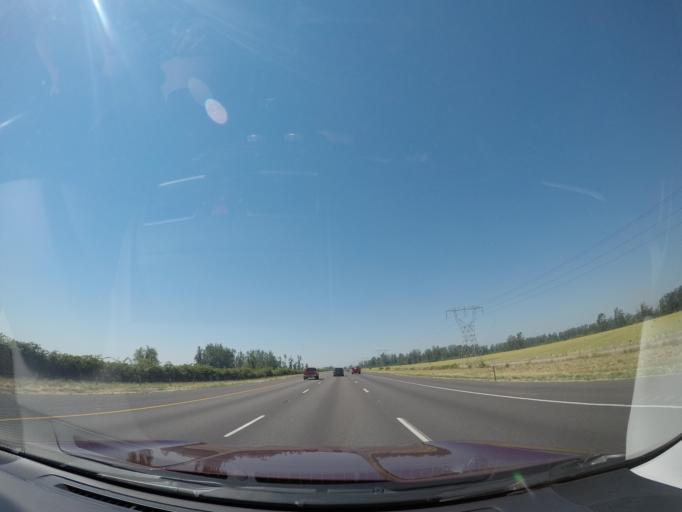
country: US
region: Oregon
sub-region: Marion County
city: Gervais
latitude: 45.1128
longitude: -122.9199
